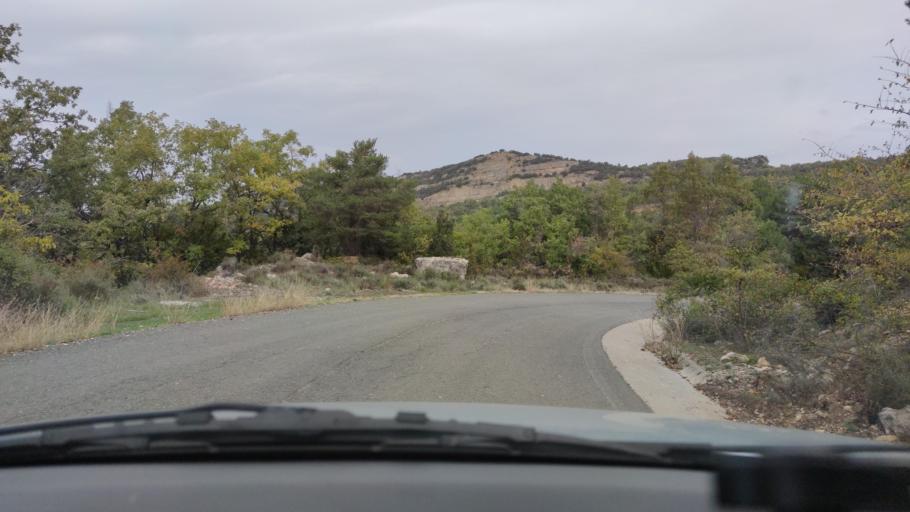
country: ES
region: Catalonia
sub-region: Provincia de Lleida
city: Llimiana
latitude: 42.0443
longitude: 1.0007
